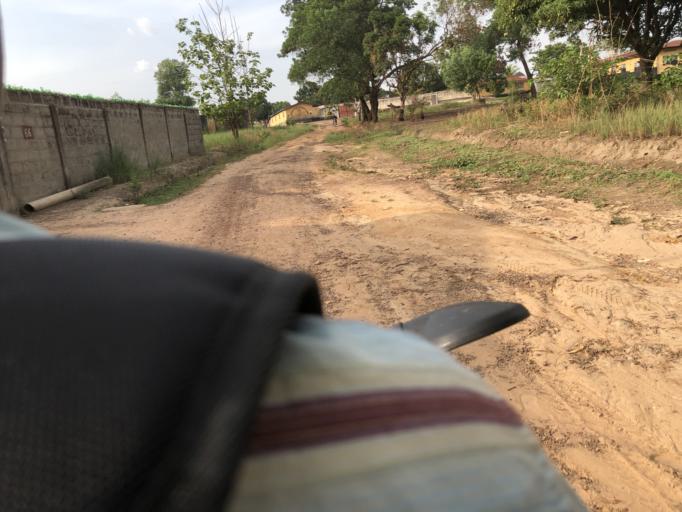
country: SL
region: Northern Province
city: Yonibana
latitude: 8.4586
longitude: -12.2026
